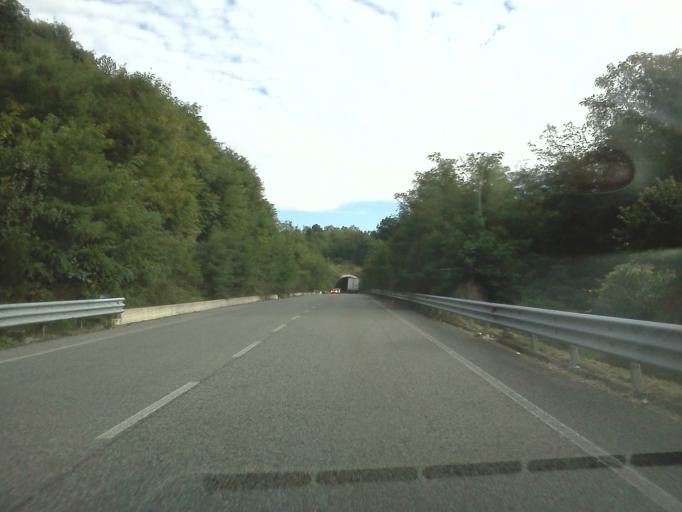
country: IT
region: Piedmont
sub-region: Provincia di Biella
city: Vallanzengo
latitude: 45.6092
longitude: 8.1608
